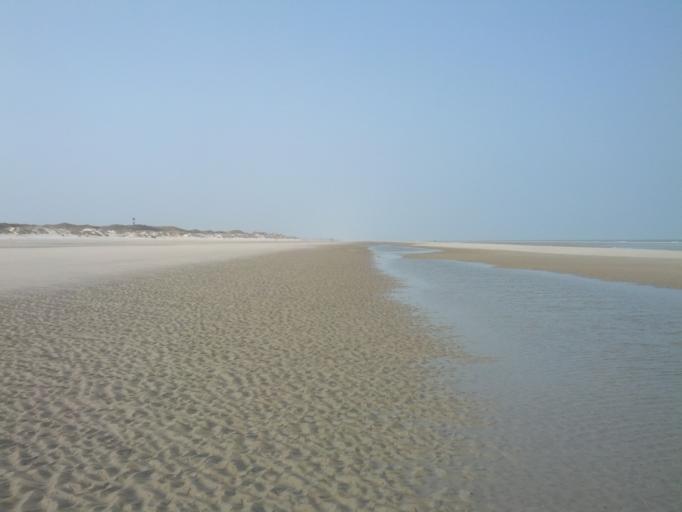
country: DE
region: Lower Saxony
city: Langeoog
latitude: 53.7599
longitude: 7.5872
